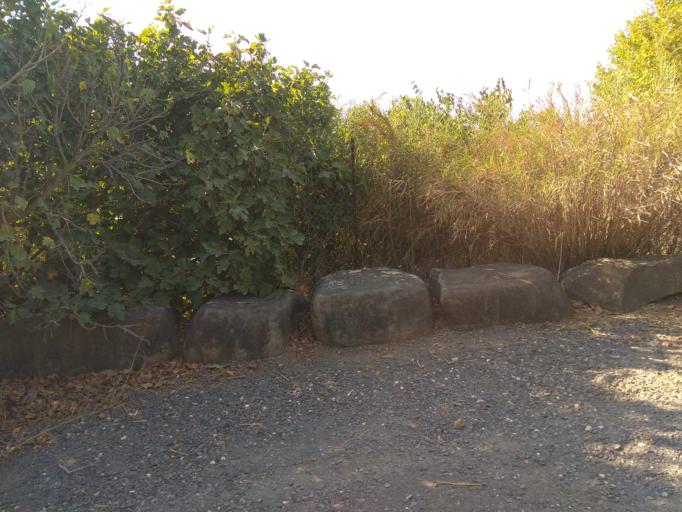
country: IL
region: Northern District
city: Qiryat Shemona
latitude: 33.2298
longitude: 35.6196
